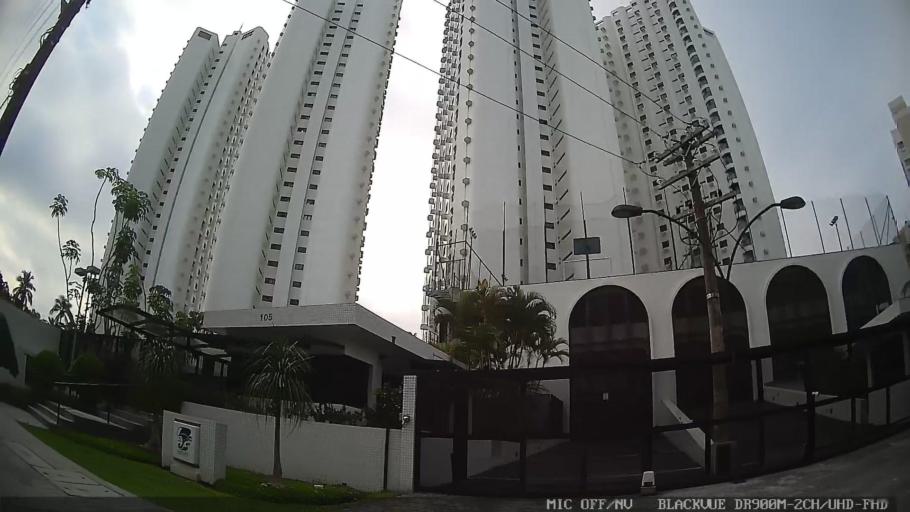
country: BR
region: Sao Paulo
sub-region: Guaruja
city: Guaruja
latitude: -23.9940
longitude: -46.1997
